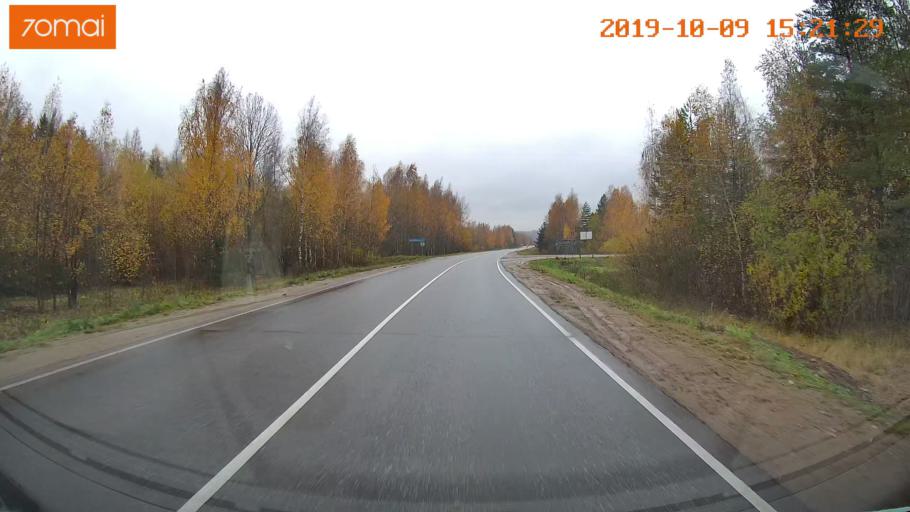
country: RU
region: Kostroma
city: Susanino
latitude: 58.0531
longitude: 41.5187
